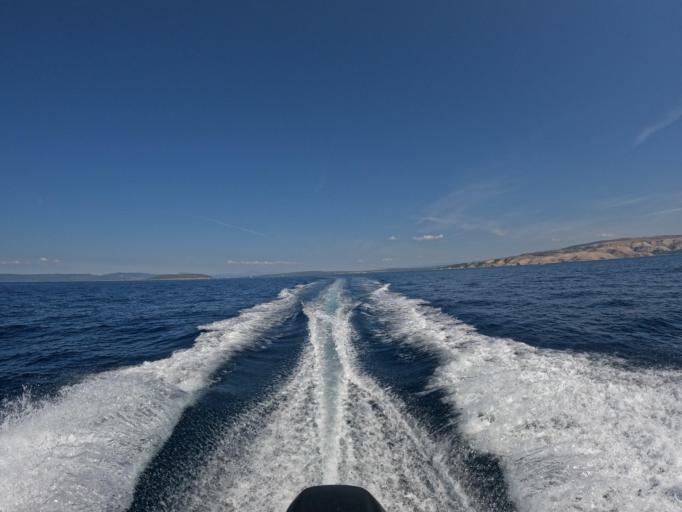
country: HR
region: Primorsko-Goranska
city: Punat
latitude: 44.9169
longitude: 14.6244
